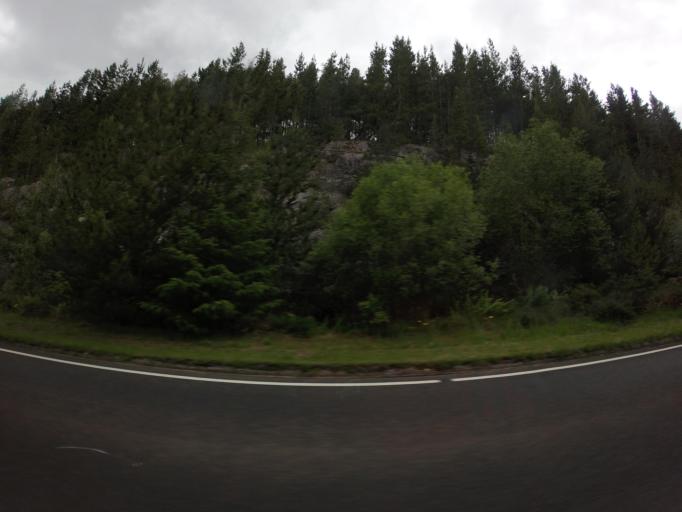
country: GB
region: Scotland
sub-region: Highland
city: Muir of Ord
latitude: 57.6291
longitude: -4.6933
